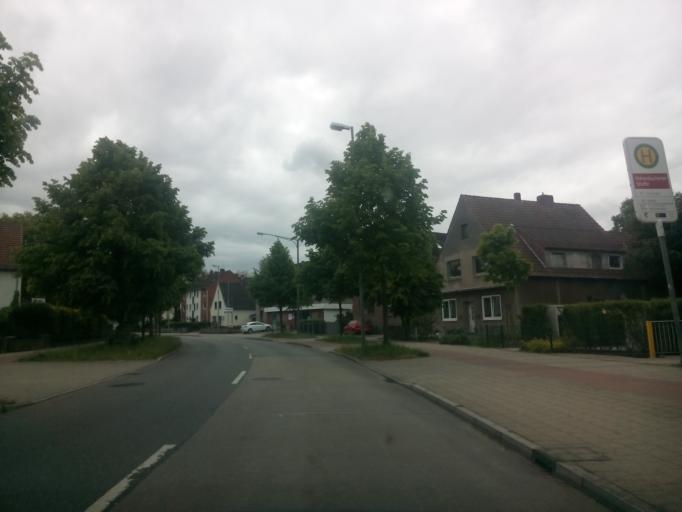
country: DE
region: Lower Saxony
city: Schwanewede
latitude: 53.2106
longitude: 8.5793
